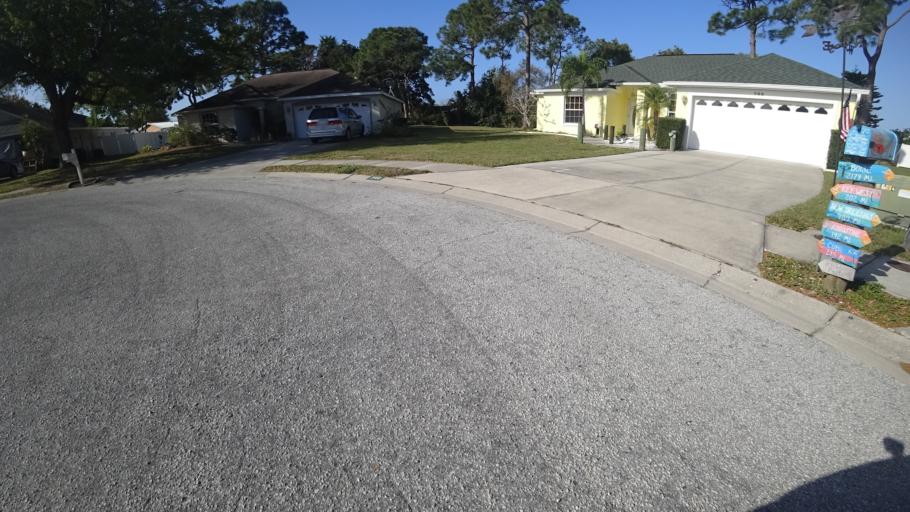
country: US
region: Florida
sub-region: Manatee County
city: Whitfield
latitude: 27.4117
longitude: -82.5587
